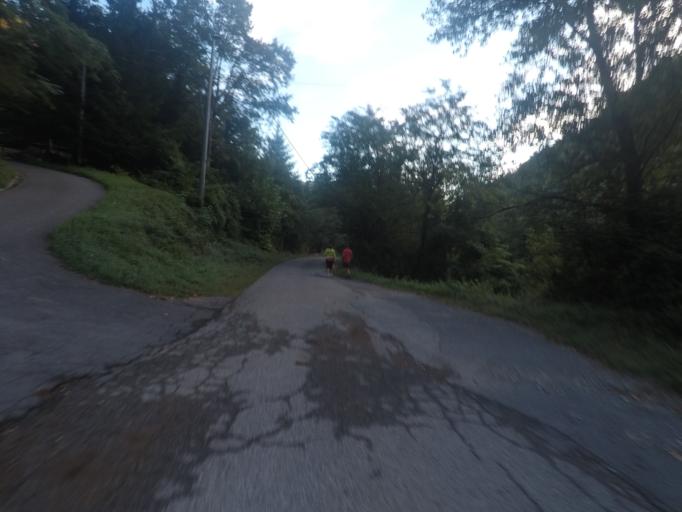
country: IT
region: Tuscany
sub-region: Provincia di Lucca
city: Pescaglia
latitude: 43.9484
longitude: 10.4137
